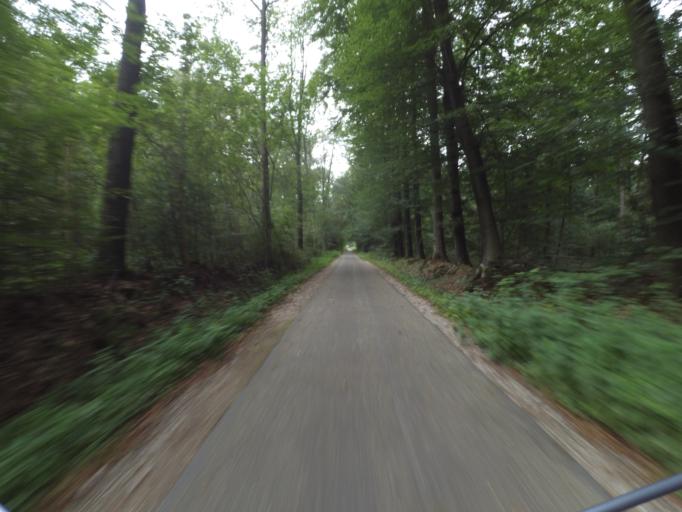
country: NL
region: Overijssel
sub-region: Gemeente Oldenzaal
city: Oldenzaal
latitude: 52.3270
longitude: 6.9628
